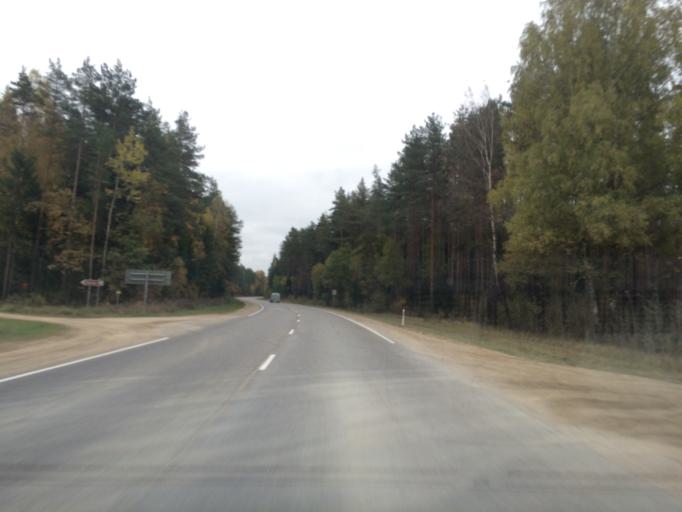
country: LV
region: Koknese
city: Koknese
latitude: 56.5993
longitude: 25.5226
